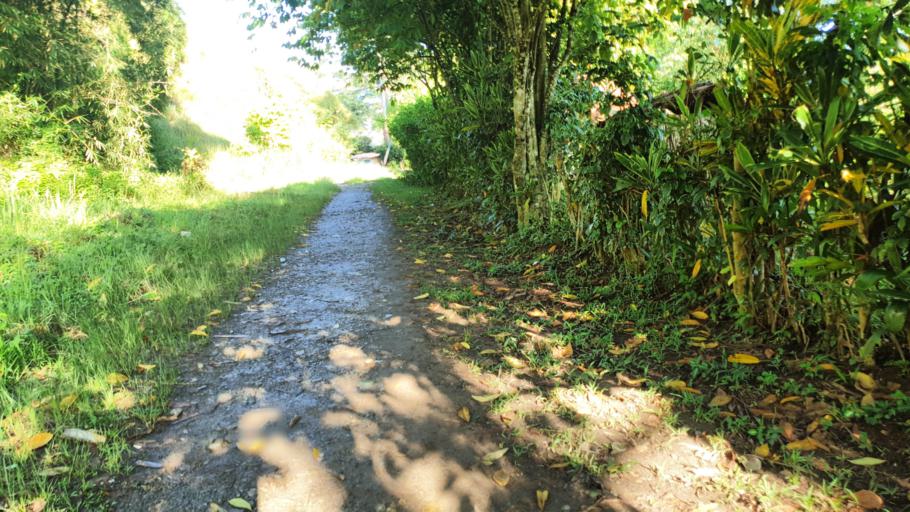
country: PG
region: Western Highlands
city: Rauna
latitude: -5.8002
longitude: 144.3611
